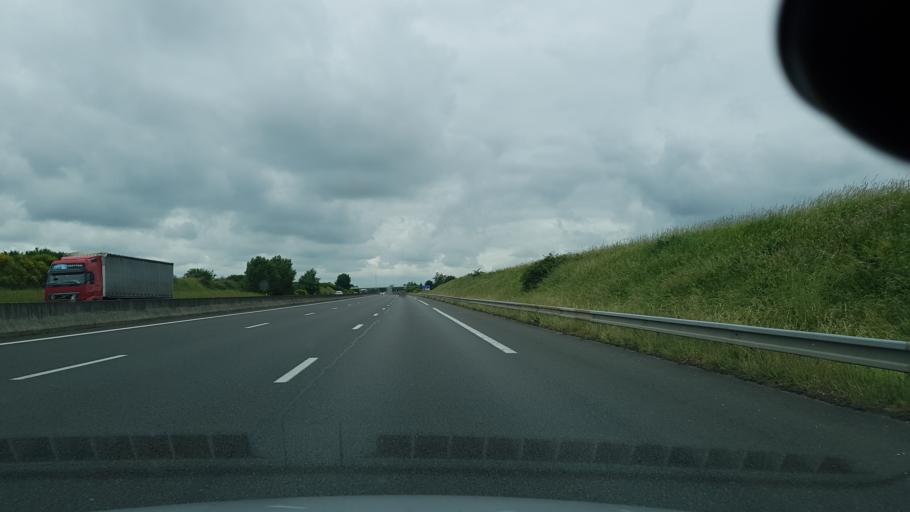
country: FR
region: Centre
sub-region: Departement du Loir-et-Cher
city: Herbault
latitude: 47.6119
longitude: 1.1414
